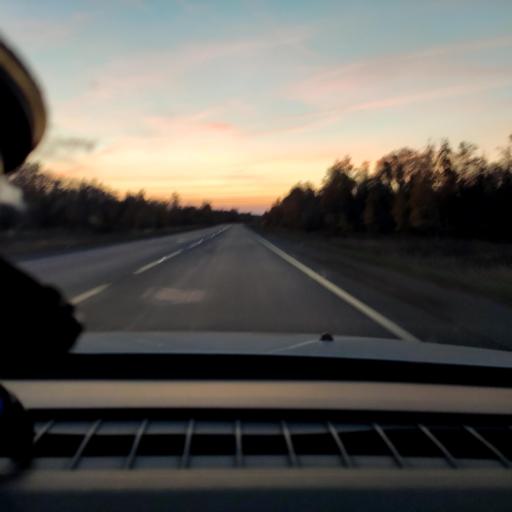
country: RU
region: Samara
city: Chapayevsk
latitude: 52.9922
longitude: 49.8347
